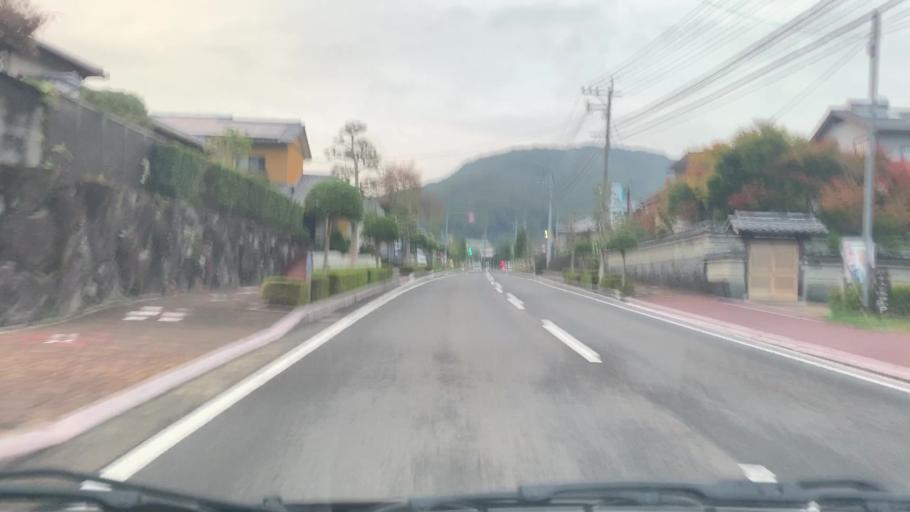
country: JP
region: Saga Prefecture
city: Ureshinomachi-shimojuku
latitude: 33.1478
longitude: 129.9002
